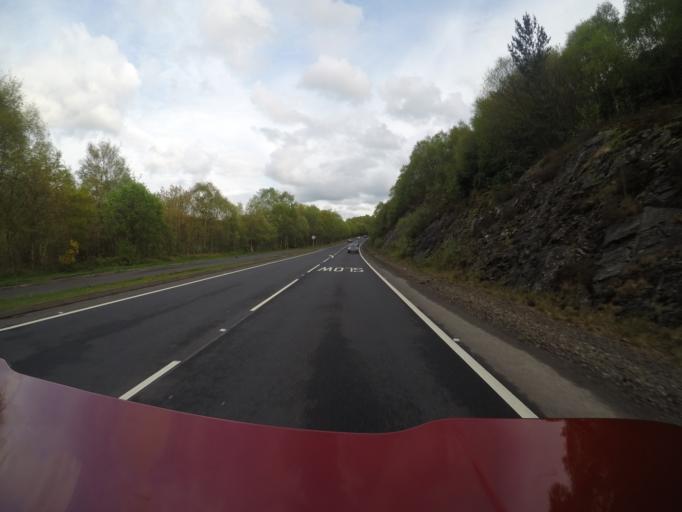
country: GB
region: Scotland
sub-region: Argyll and Bute
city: Helensburgh
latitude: 56.1663
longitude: -4.6676
